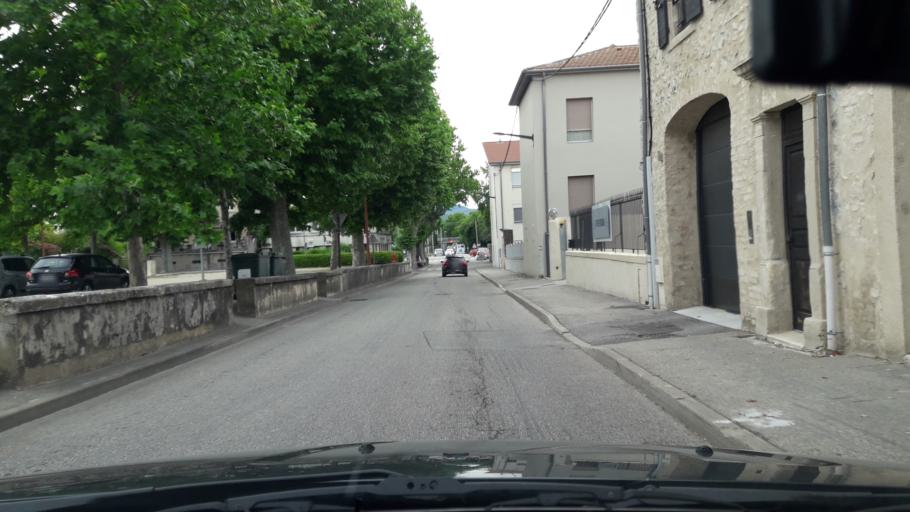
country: FR
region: Rhone-Alpes
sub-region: Departement de la Drome
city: Loriol-sur-Drome
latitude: 44.7528
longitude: 4.8195
